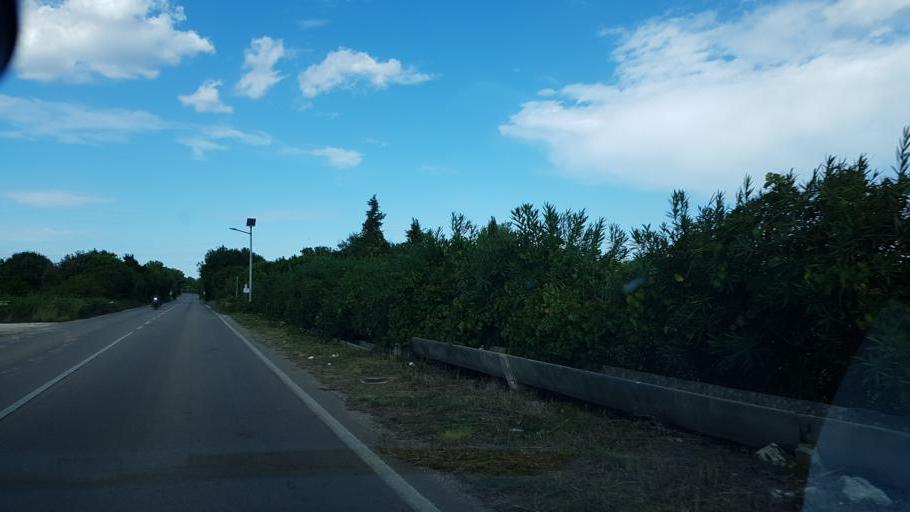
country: IT
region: Apulia
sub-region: Provincia di Lecce
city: Borgagne
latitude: 40.2353
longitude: 18.4440
